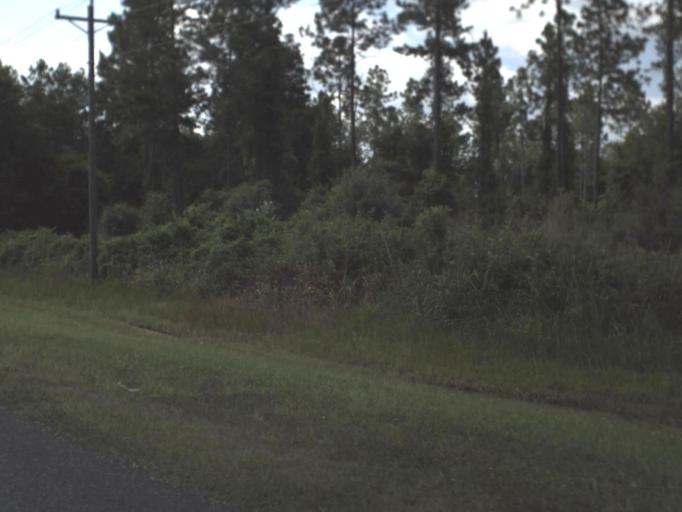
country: US
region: Florida
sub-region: Alachua County
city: Waldo
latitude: 29.7639
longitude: -82.1442
